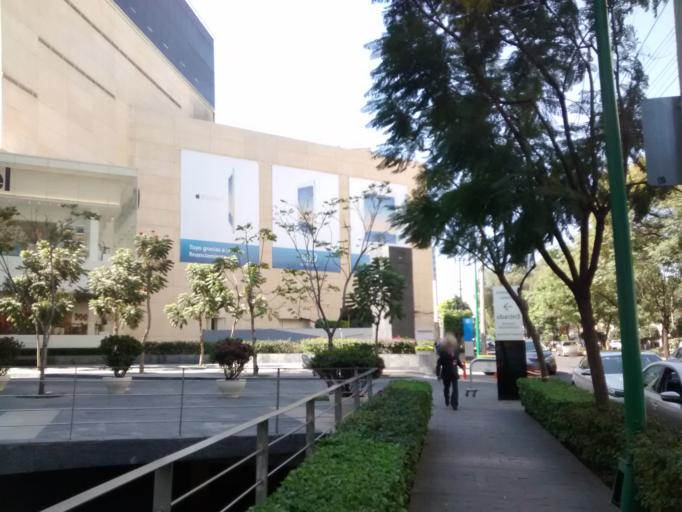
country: MX
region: Mexico City
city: Miguel Hidalgo
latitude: 19.4400
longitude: -99.2032
